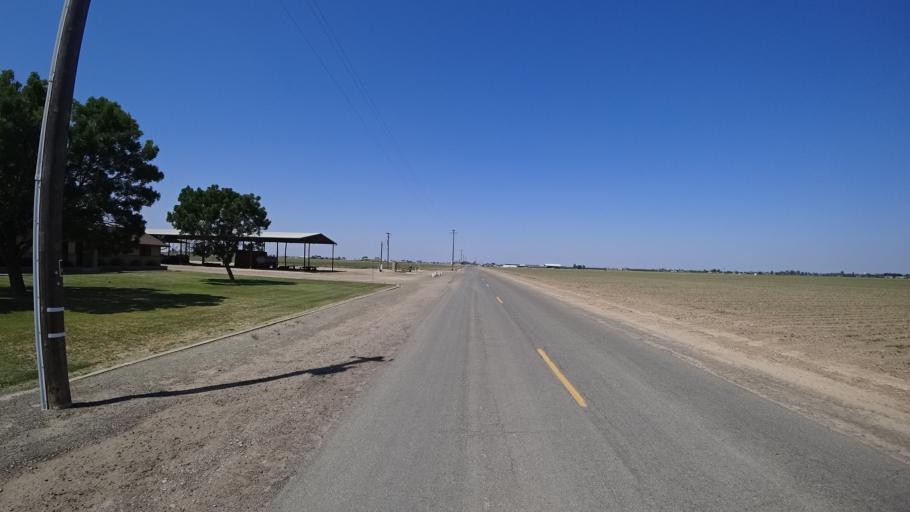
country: US
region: California
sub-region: Kings County
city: Home Garden
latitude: 36.2839
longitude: -119.6046
